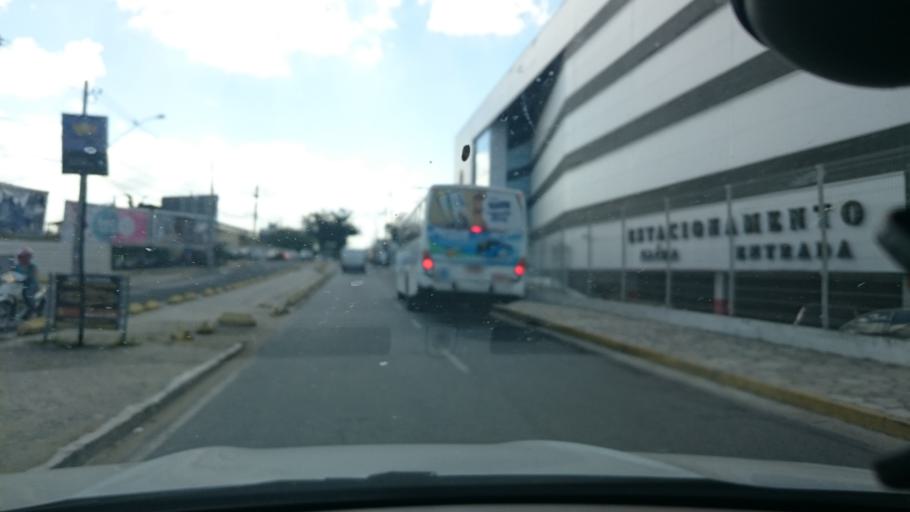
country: BR
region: Paraiba
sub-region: Campina Grande
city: Campina Grande
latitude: -7.2367
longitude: -35.8707
